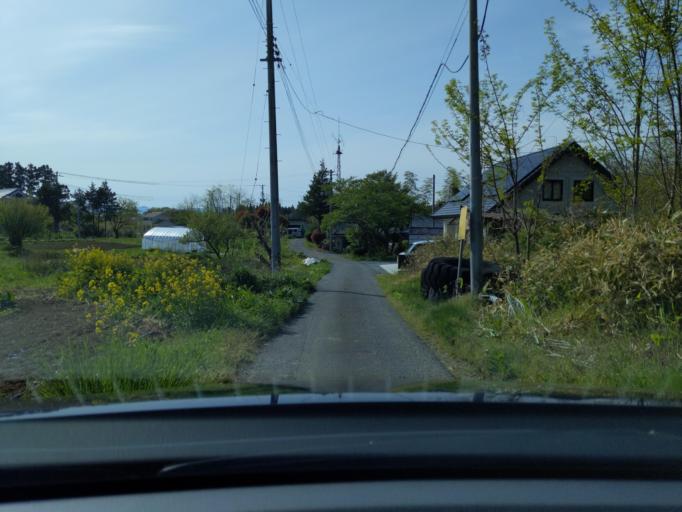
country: JP
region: Fukushima
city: Sukagawa
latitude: 37.3103
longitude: 140.4201
